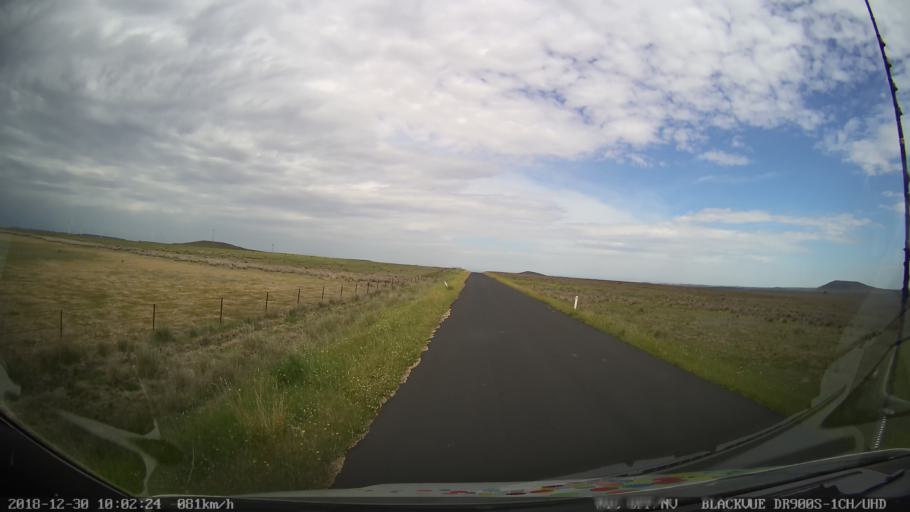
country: AU
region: New South Wales
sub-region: Cooma-Monaro
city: Cooma
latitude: -36.5157
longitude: 149.1725
